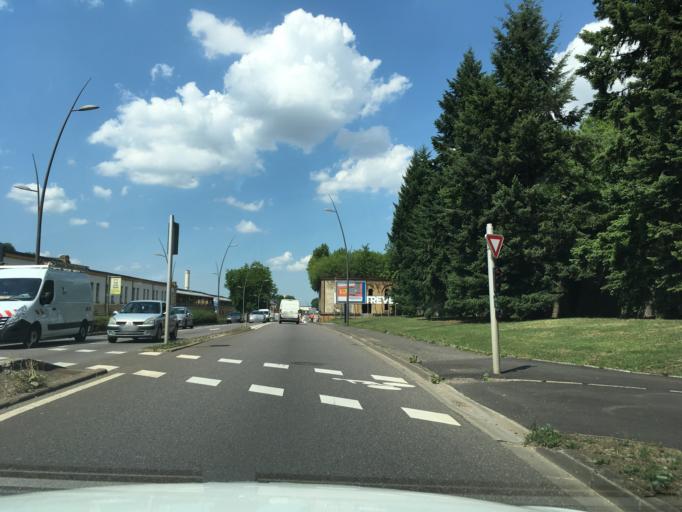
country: FR
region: Lorraine
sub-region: Departement de la Moselle
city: Metz
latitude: 49.1197
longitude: 6.1888
